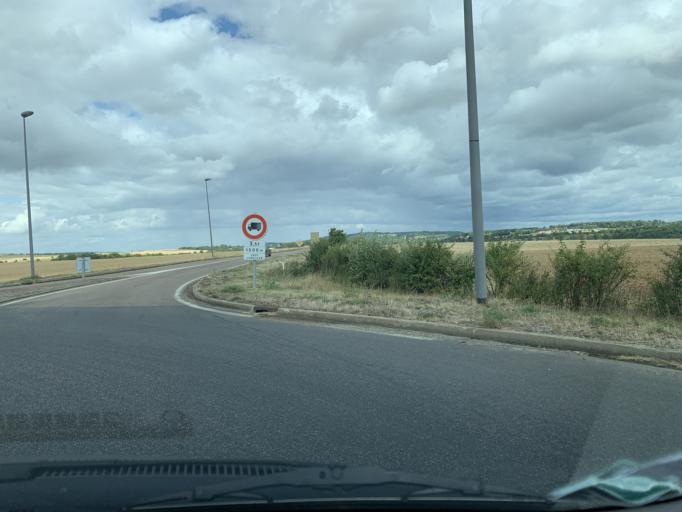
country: FR
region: Bourgogne
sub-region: Departement de la Nievre
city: Clamecy
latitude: 47.4392
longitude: 3.4906
